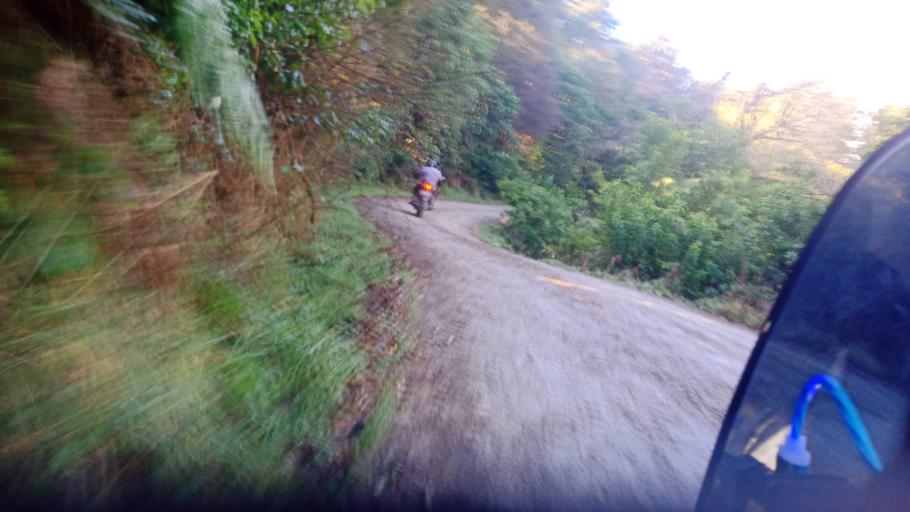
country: NZ
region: Hawke's Bay
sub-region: Wairoa District
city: Wairoa
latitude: -38.6673
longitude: 177.5408
